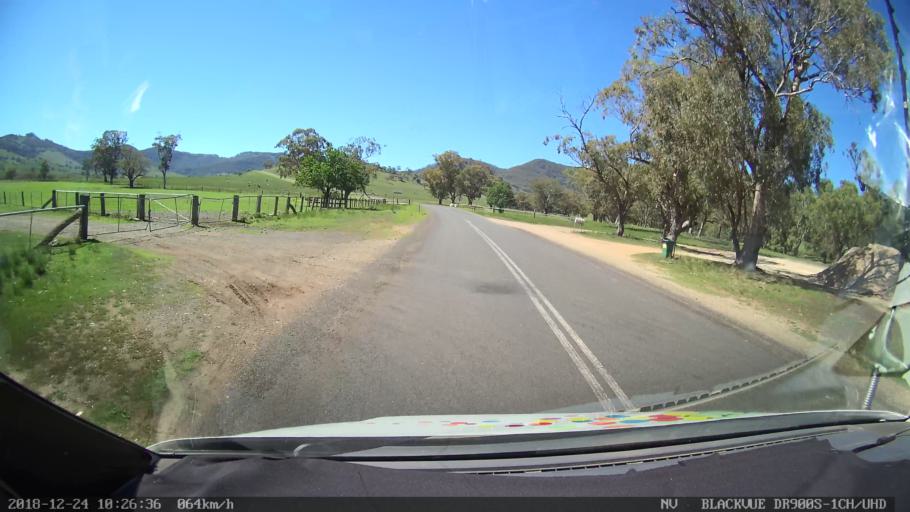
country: AU
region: New South Wales
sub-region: Liverpool Plains
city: Quirindi
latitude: -31.8109
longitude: 150.5272
